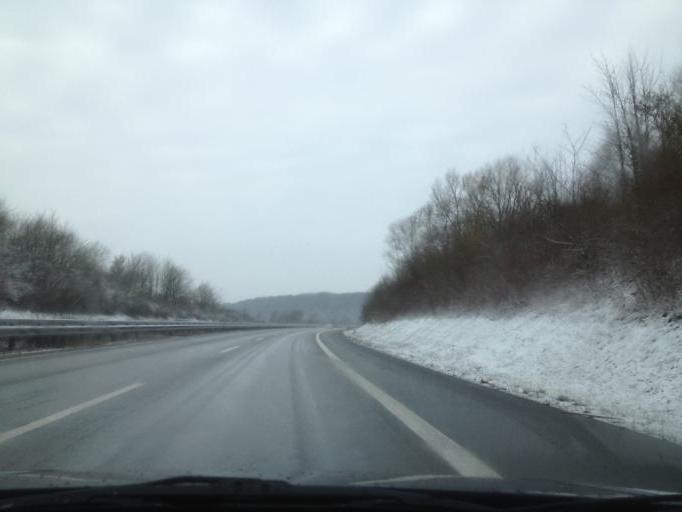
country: DE
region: Rheinland-Pfalz
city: Kleinsteinhausen
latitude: 49.2180
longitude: 7.4525
